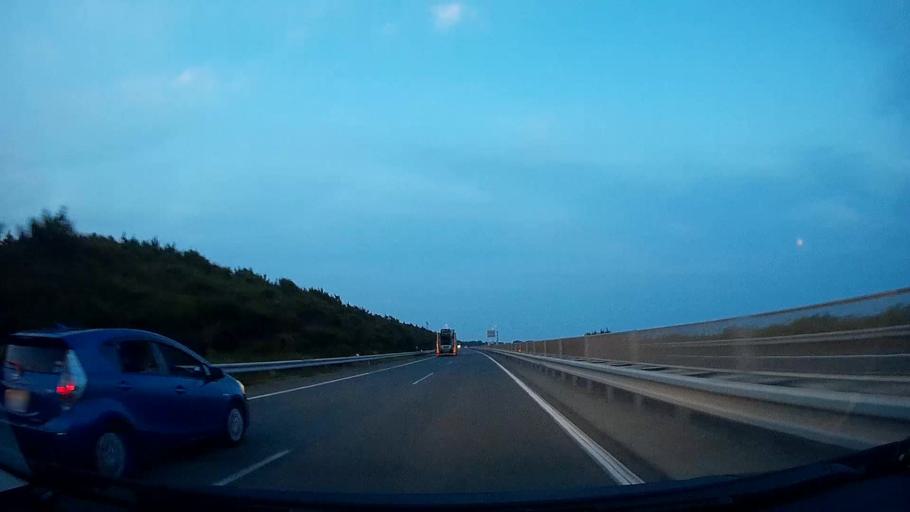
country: JP
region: Shizuoka
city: Kosai-shi
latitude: 34.6806
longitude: 137.5736
